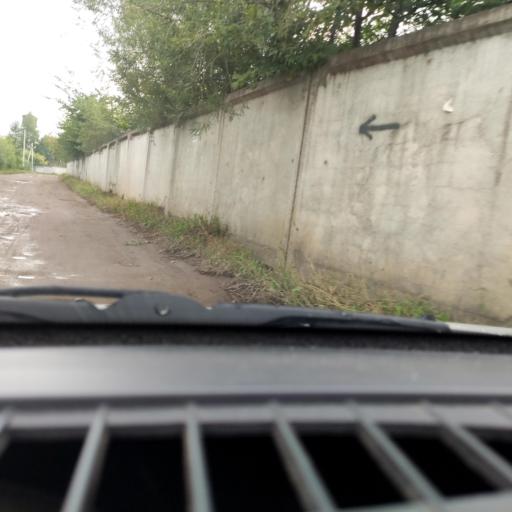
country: RU
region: Perm
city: Kondratovo
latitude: 58.0102
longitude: 56.0747
